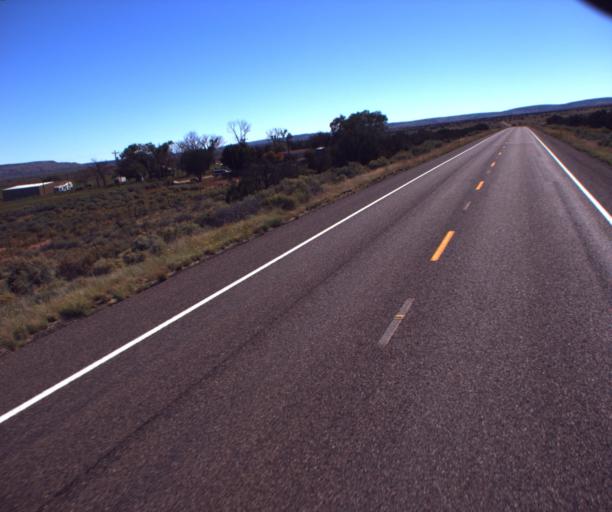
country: US
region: Arizona
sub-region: Apache County
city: Saint Johns
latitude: 34.6179
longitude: -109.6592
